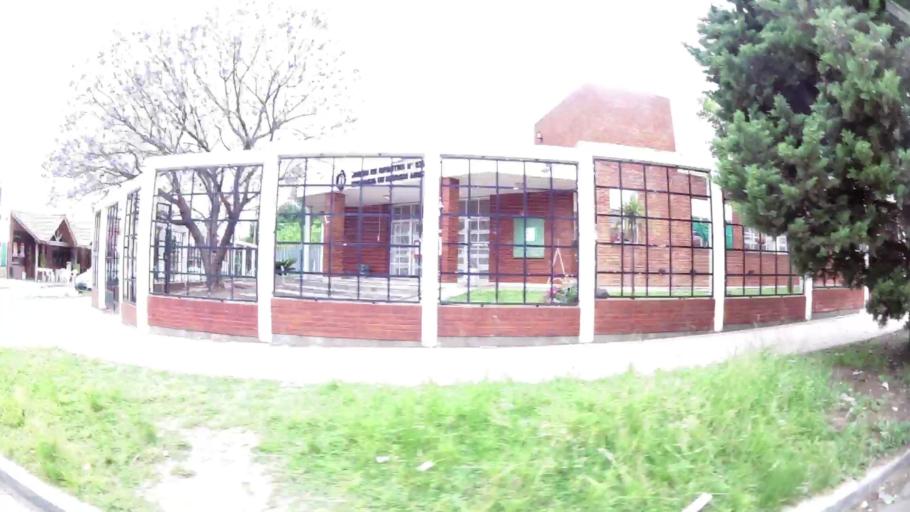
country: AR
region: Buenos Aires
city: San Justo
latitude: -34.7194
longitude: -58.5227
